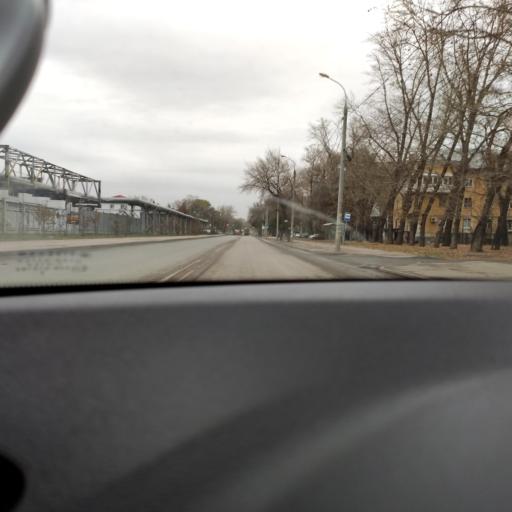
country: RU
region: Samara
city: Smyshlyayevka
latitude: 53.2121
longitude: 50.2963
